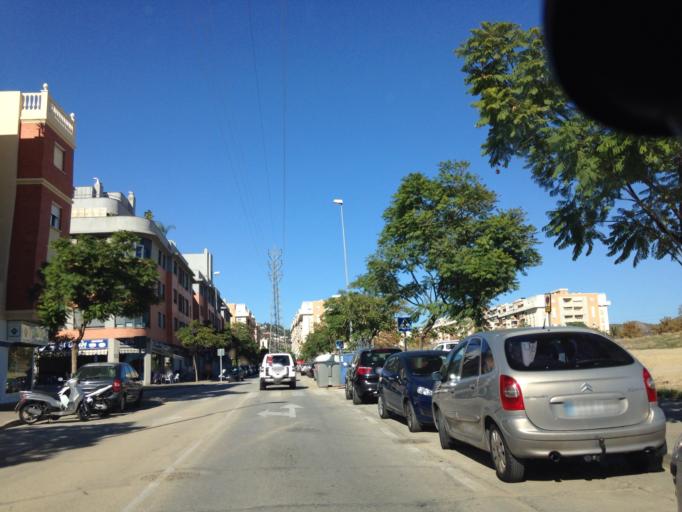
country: ES
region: Andalusia
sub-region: Provincia de Malaga
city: Malaga
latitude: 36.7228
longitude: -4.4746
